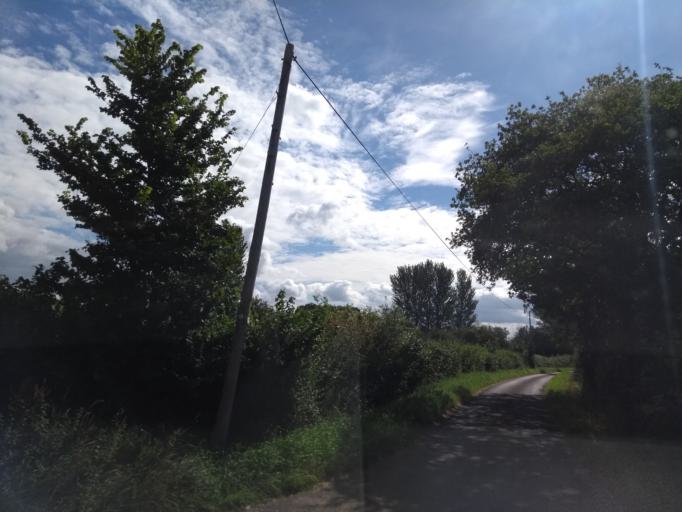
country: GB
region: England
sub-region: Somerset
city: Creech Saint Michael
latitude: 51.0384
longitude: -3.0178
